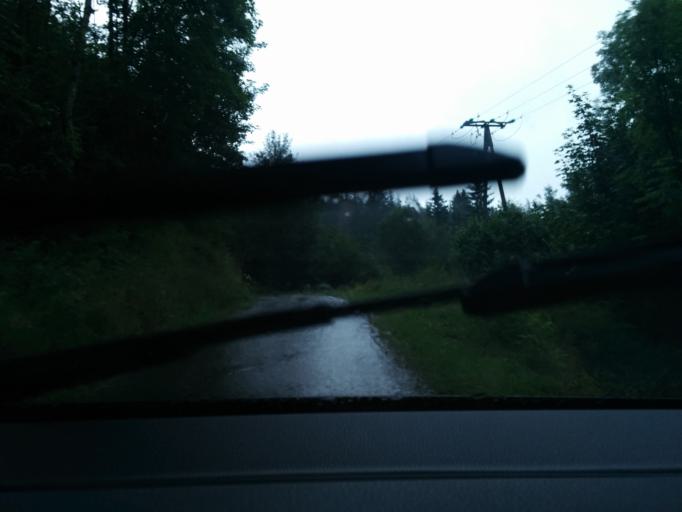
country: FR
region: Franche-Comte
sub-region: Departement du Jura
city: Valfin-les-Saint-Claude
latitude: 46.4599
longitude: 5.8413
